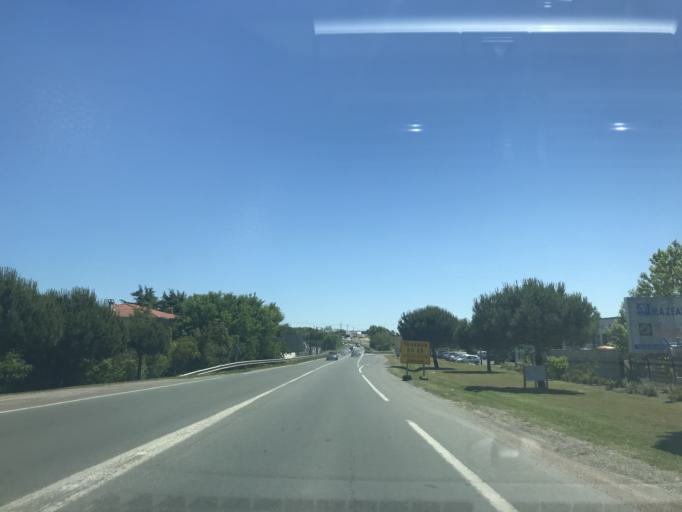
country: FR
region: Poitou-Charentes
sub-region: Departement de la Charente-Maritime
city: Vaux-sur-Mer
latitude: 45.6479
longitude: -1.0467
